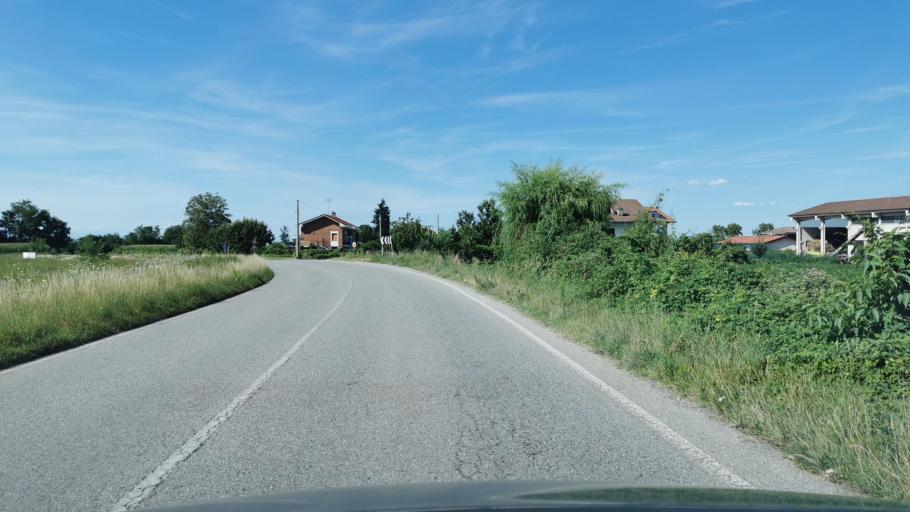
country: IT
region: Piedmont
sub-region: Provincia di Cuneo
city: Cuneo
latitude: 44.3631
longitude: 7.5608
